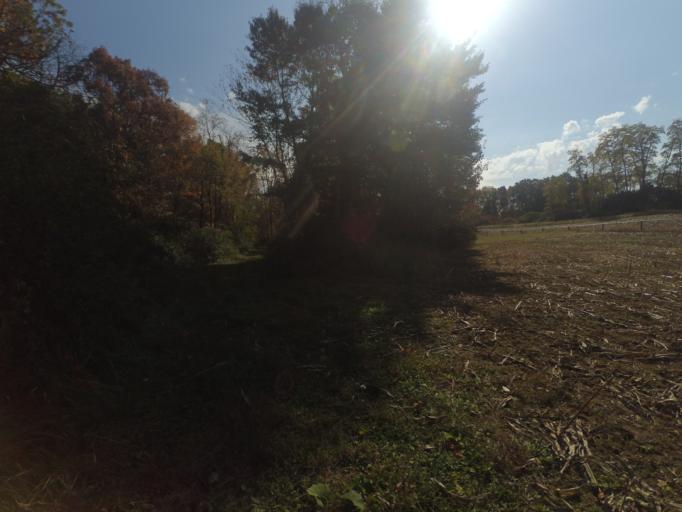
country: US
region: Pennsylvania
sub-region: Centre County
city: Park Forest Village
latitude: 40.8347
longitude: -77.8925
